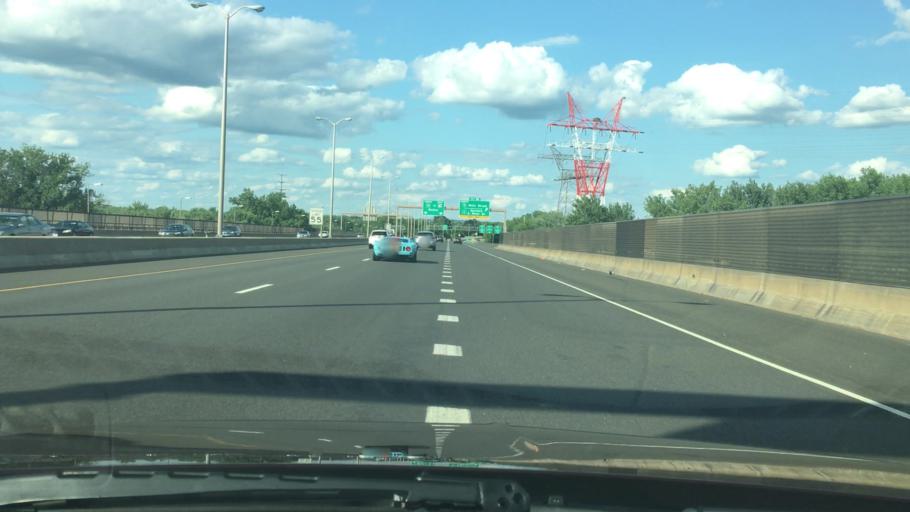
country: US
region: Connecticut
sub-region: Hartford County
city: Hartford
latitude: 41.7528
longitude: -72.6527
